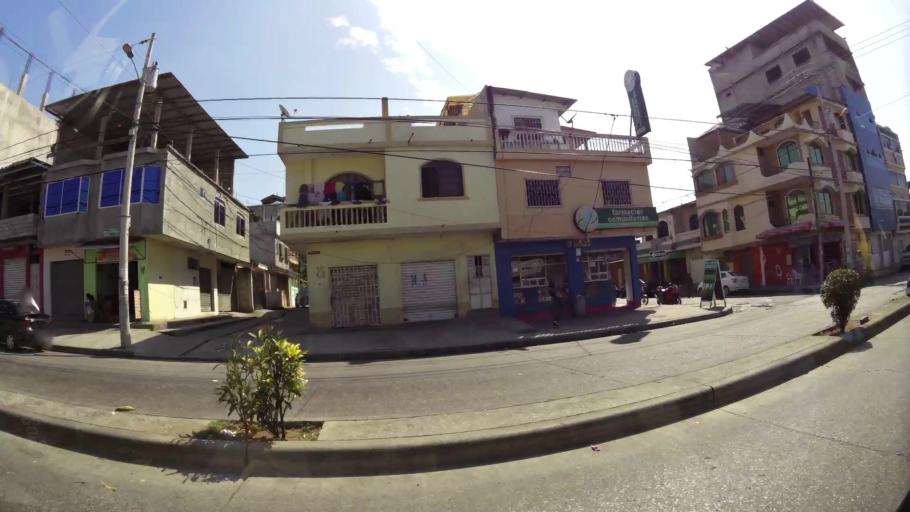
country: EC
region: Guayas
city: Eloy Alfaro
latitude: -2.1204
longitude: -79.9085
